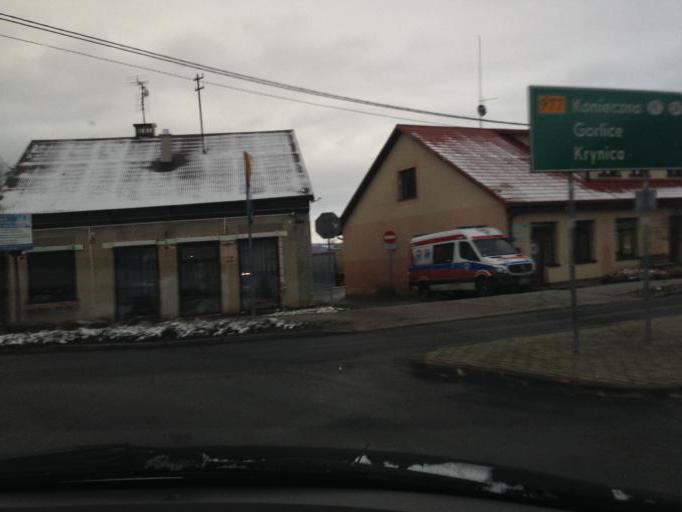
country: PL
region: Lesser Poland Voivodeship
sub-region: Powiat tarnowski
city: Gromnik
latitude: 49.8381
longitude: 20.9613
